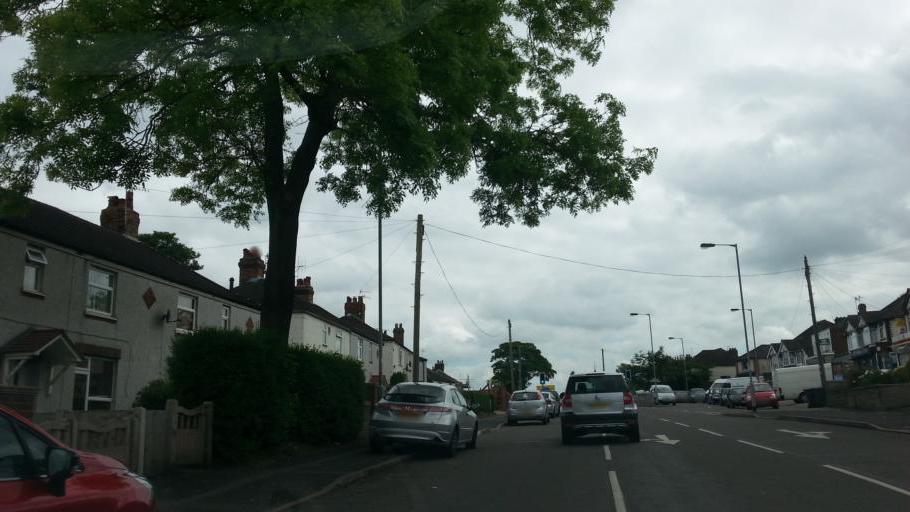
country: GB
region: England
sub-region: Staffordshire
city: Newcastle under Lyme
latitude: 53.0255
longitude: -2.2330
